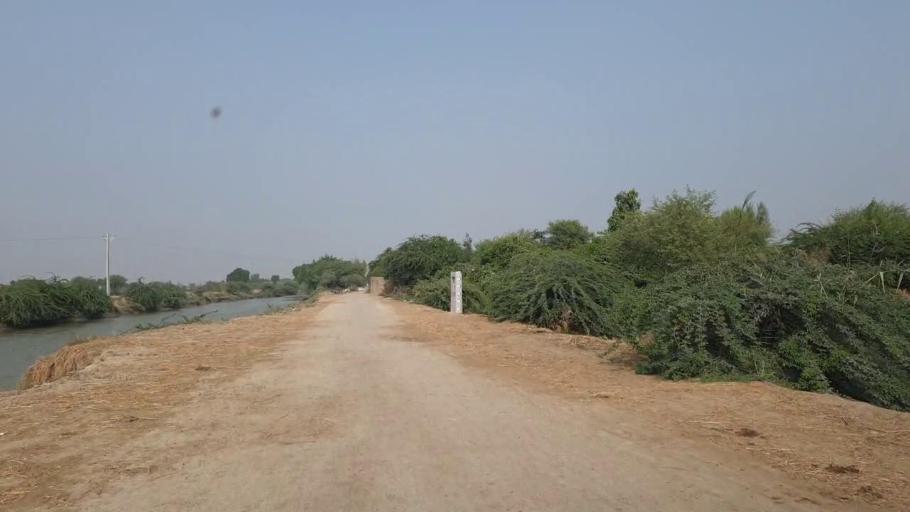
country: PK
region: Sindh
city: Kario
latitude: 24.9226
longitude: 68.6010
